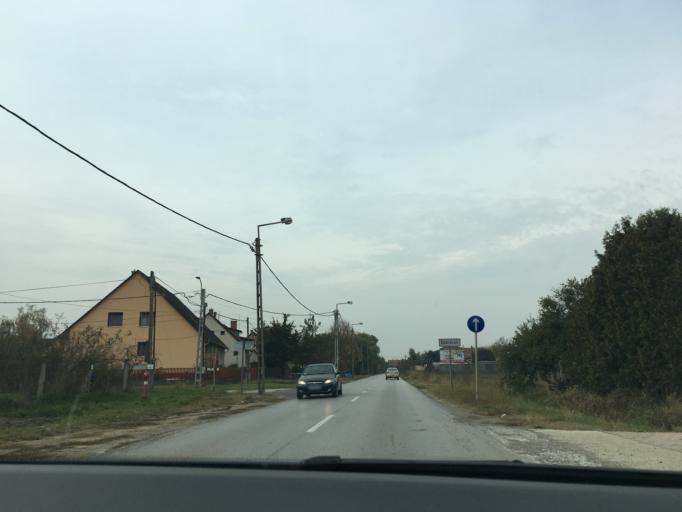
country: HU
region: Hajdu-Bihar
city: Debrecen
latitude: 47.5498
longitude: 21.6772
